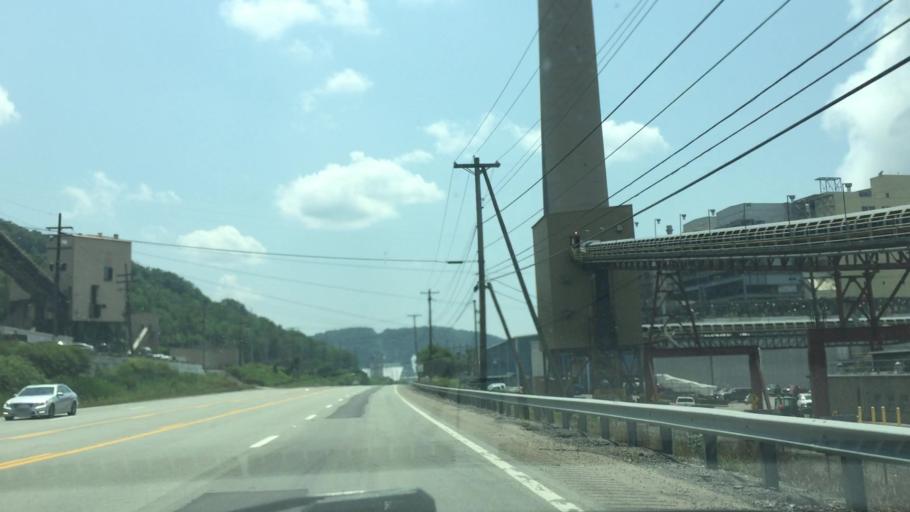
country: US
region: Ohio
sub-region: Belmont County
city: Powhatan Point
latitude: 39.8331
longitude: -80.8149
